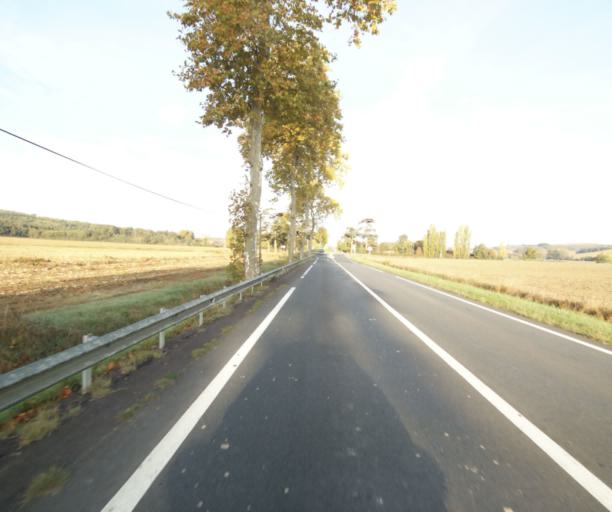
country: FR
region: Midi-Pyrenees
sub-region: Departement du Tarn-et-Garonne
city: Saint-Nauphary
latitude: 43.9434
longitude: 1.4652
